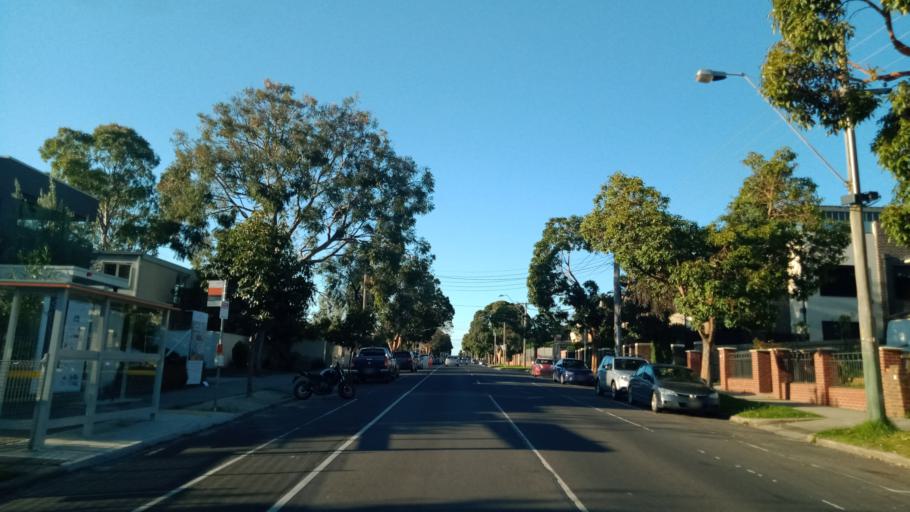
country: AU
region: Victoria
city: Glenferrie
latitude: -37.8393
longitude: 145.0461
